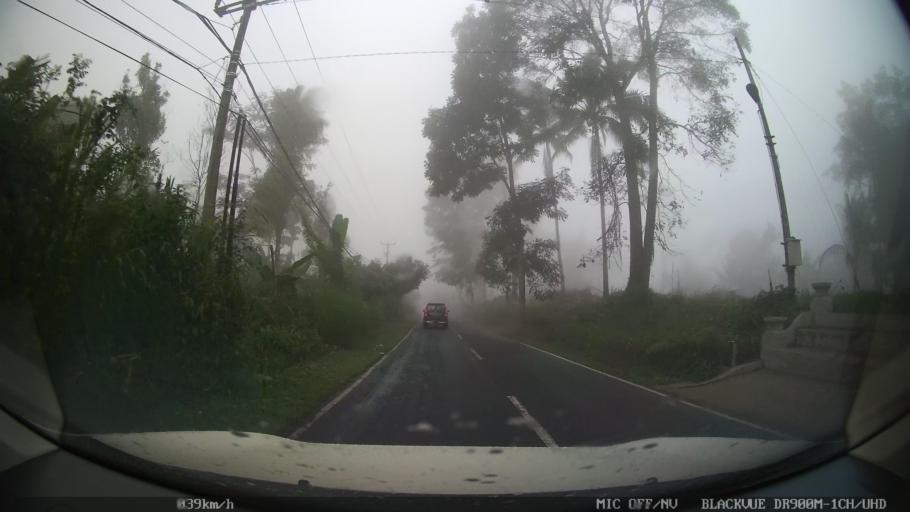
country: ID
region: Bali
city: Banjar Taro Kelod
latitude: -8.3379
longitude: 115.2830
